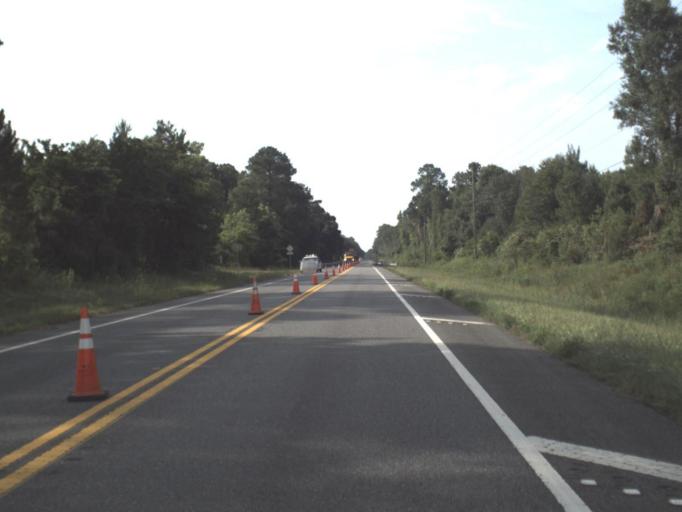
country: US
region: Florida
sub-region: Taylor County
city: Perry
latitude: 30.1889
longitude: -83.6028
